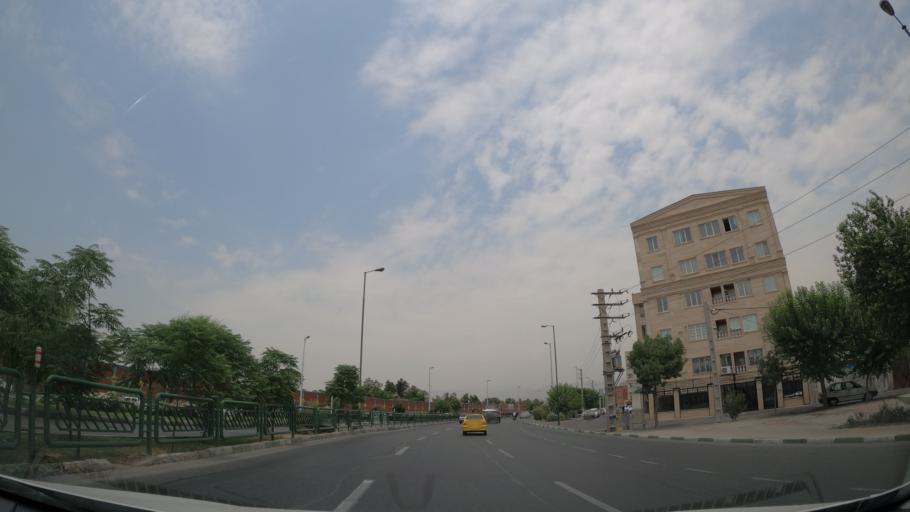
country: IR
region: Tehran
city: Tehran
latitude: 35.6845
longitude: 51.3424
